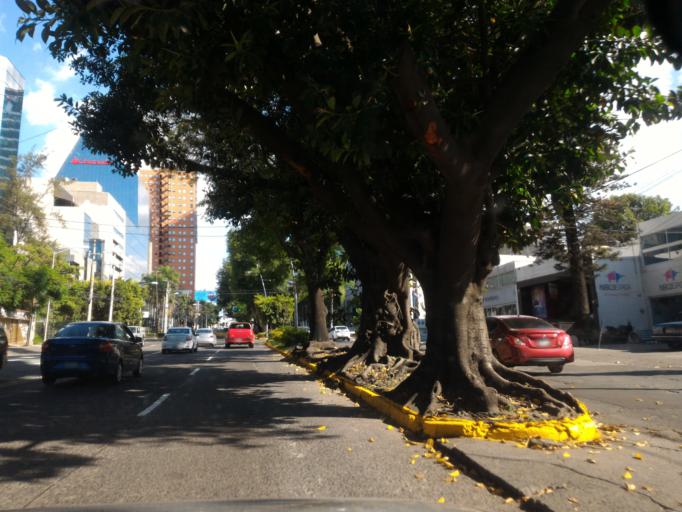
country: MX
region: Jalisco
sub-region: Zapopan
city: Zapopan
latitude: 20.7048
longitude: -103.3768
